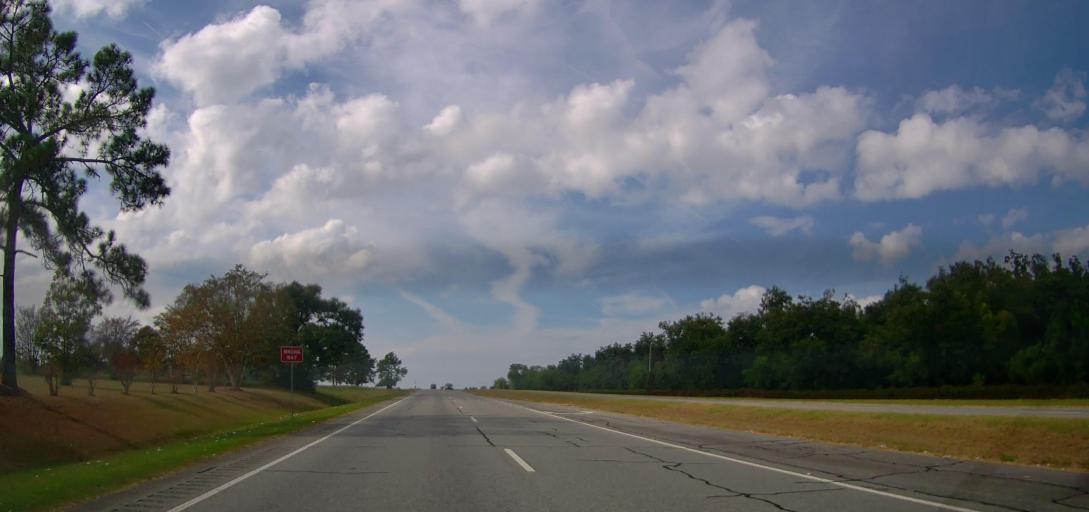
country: US
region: Georgia
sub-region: Thomas County
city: Meigs
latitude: 31.1065
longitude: -84.1136
